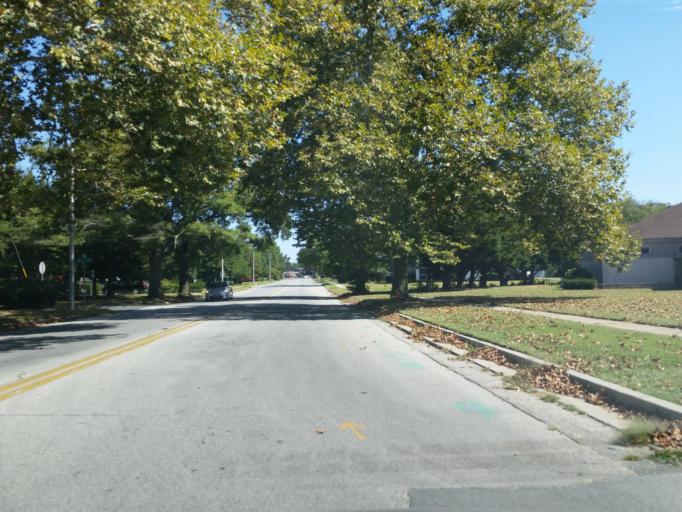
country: US
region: Maryland
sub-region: Wicomico County
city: Salisbury
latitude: 38.3704
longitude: -75.5796
